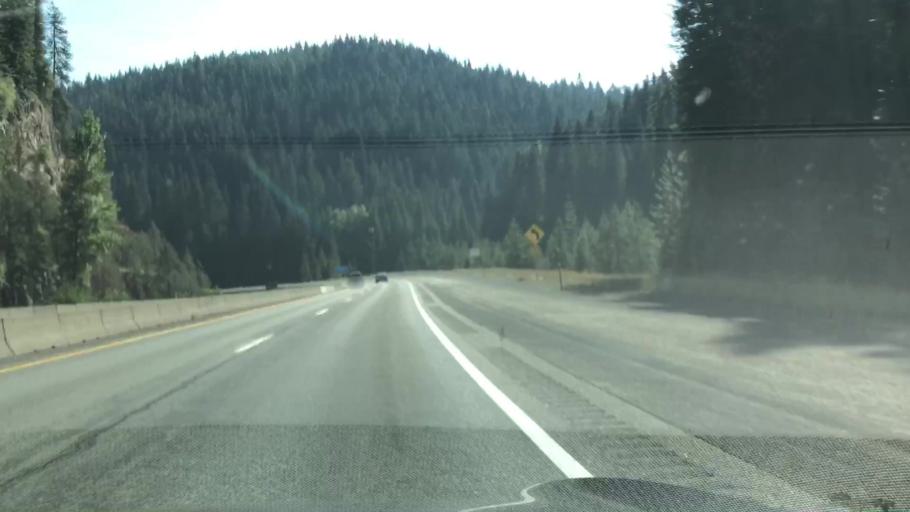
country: US
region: Idaho
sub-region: Shoshone County
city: Pinehurst
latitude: 47.5950
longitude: -116.4925
